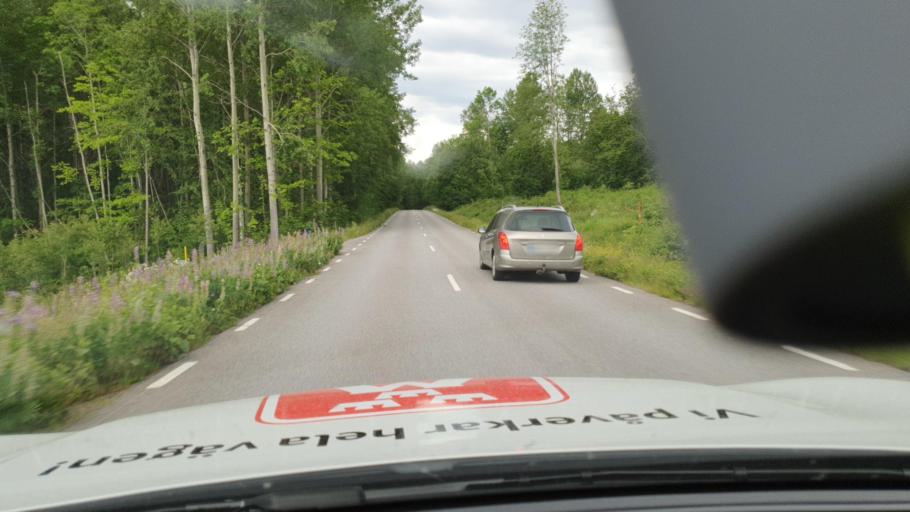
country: SE
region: Vaestra Goetaland
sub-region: Karlsborgs Kommun
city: Karlsborg
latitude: 58.7561
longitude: 14.5099
